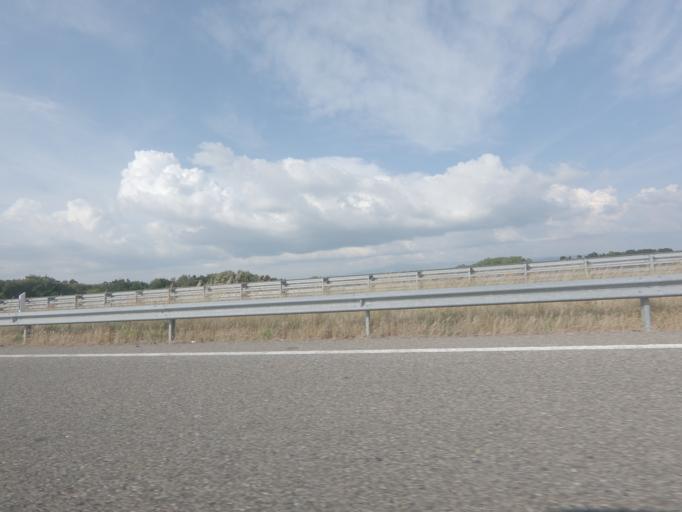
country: ES
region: Galicia
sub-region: Provincia de Ourense
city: Xinzo de Limia
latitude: 42.1008
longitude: -7.7303
